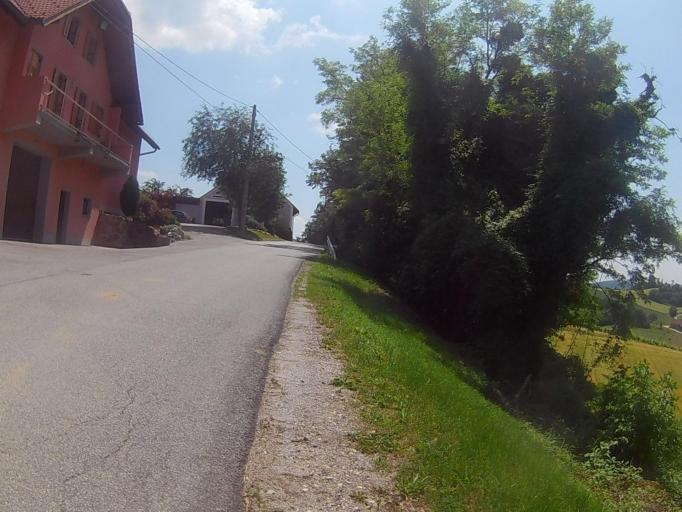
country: SI
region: Pesnica
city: Pesnica pri Mariboru
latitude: 46.5726
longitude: 15.6981
